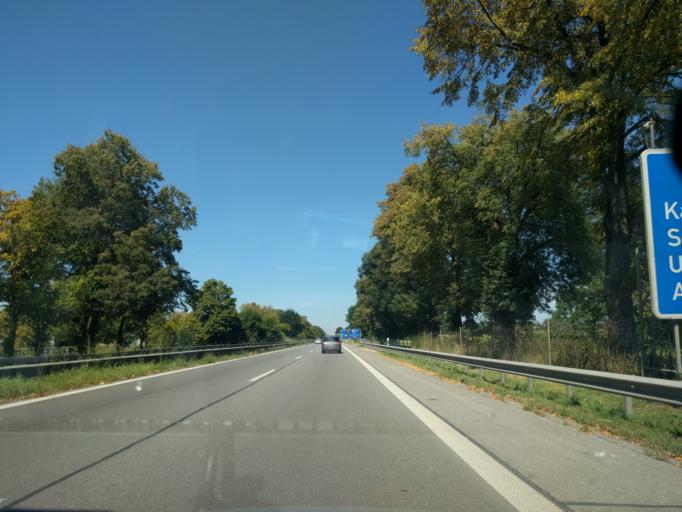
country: DE
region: Bavaria
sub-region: Upper Bavaria
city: Pasing
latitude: 48.1679
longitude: 11.4532
